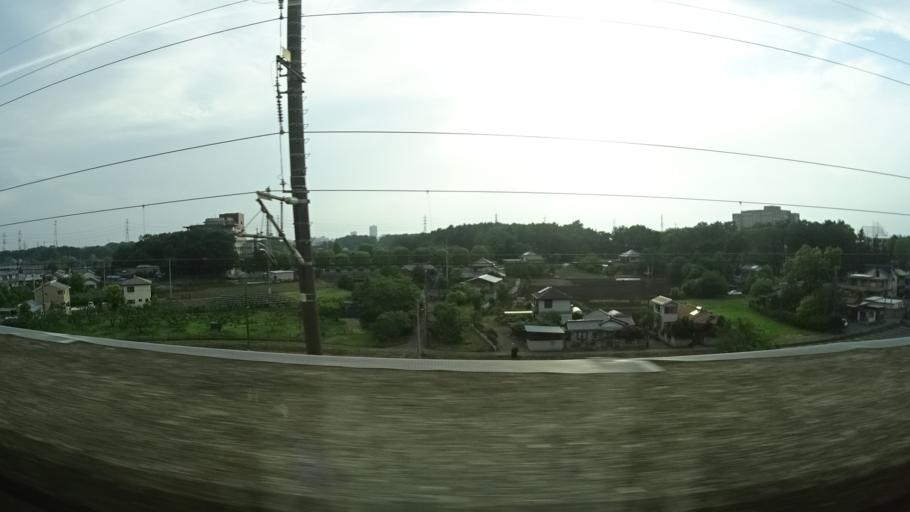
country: JP
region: Saitama
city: Ageoshimo
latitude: 35.9821
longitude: 139.6247
